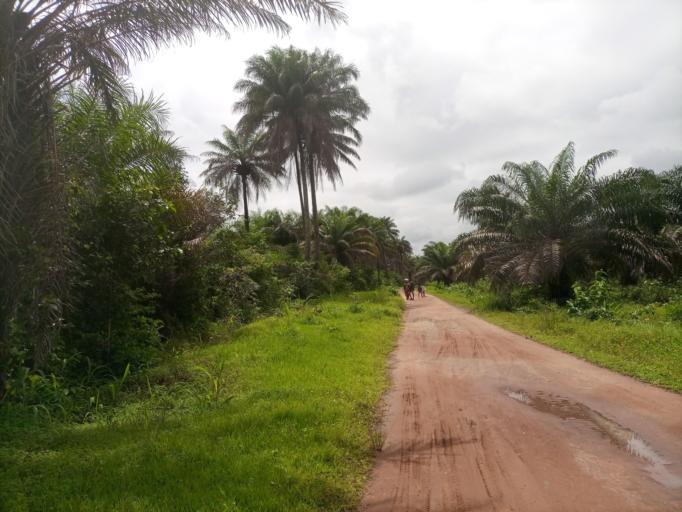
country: SL
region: Northern Province
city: Sawkta
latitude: 8.6546
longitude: -13.1802
